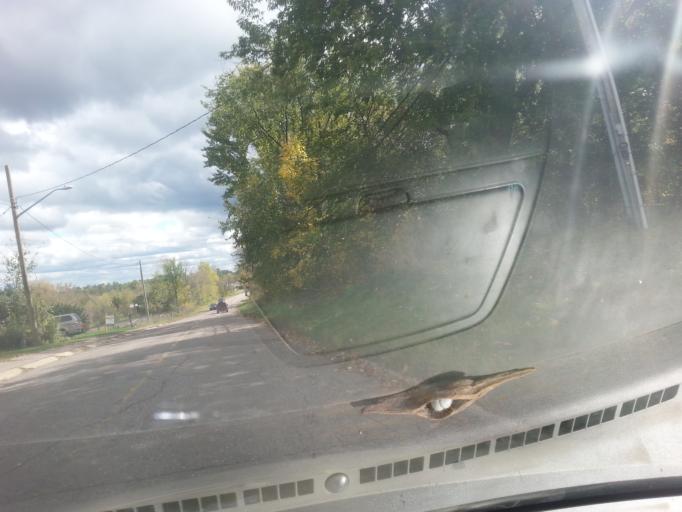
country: CA
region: Ontario
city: Pembroke
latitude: 45.5341
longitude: -77.0945
